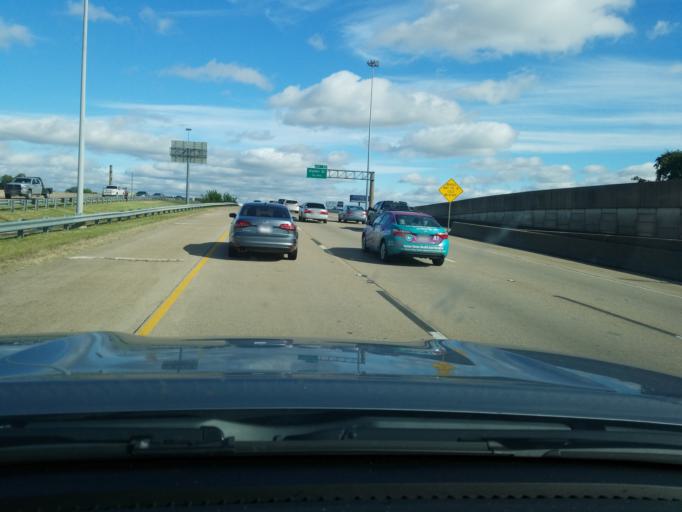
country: US
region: Texas
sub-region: Tarrant County
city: Westworth
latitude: 32.7340
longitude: -97.4063
